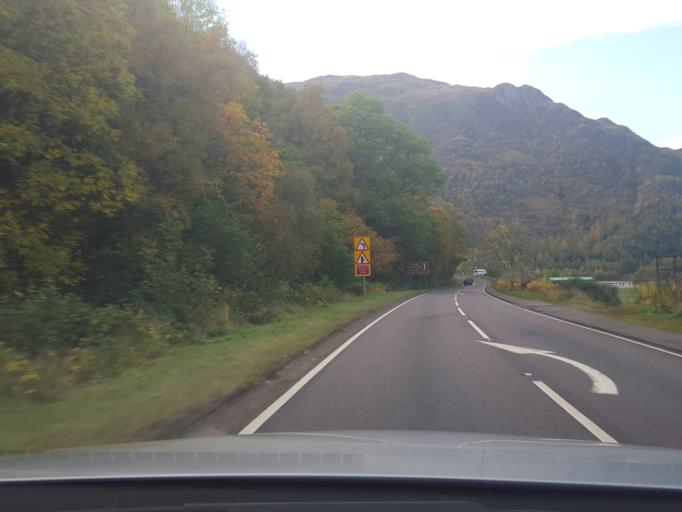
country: GB
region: Scotland
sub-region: Highland
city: Fort William
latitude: 57.2177
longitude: -5.4197
